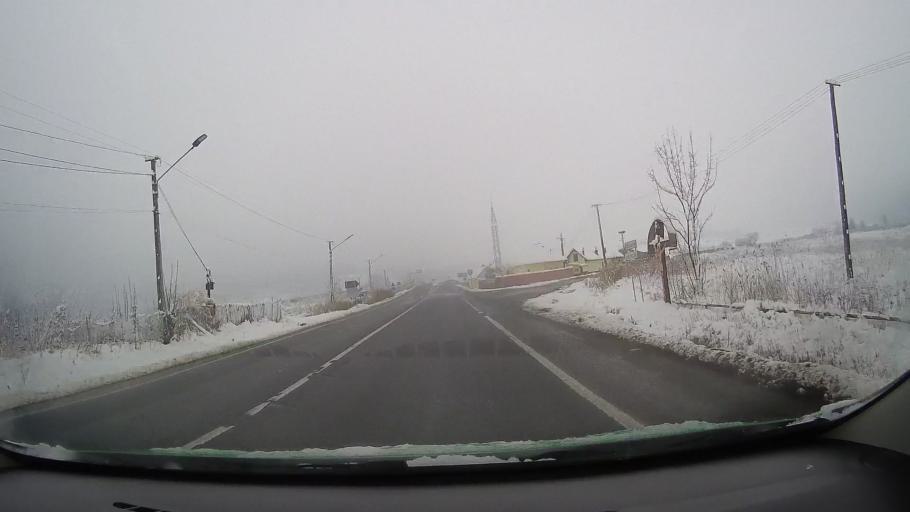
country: RO
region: Sibiu
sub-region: Comuna Orlat
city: Orlat
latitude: 45.7824
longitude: 23.9435
